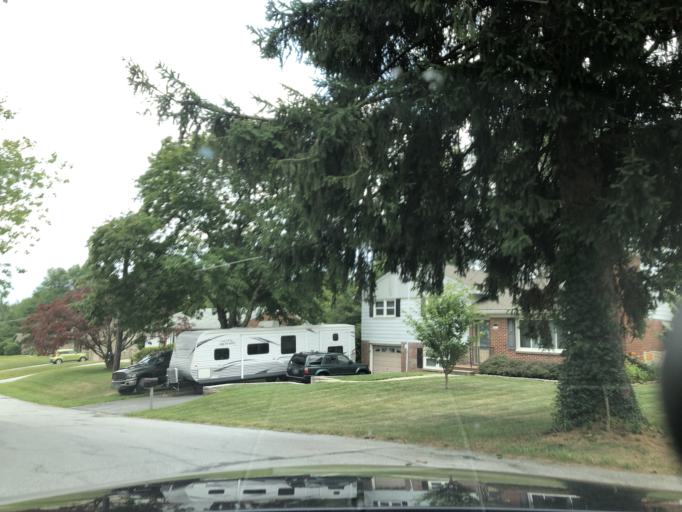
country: US
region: Maryland
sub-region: Carroll County
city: Westminster
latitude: 39.5512
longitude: -76.9892
